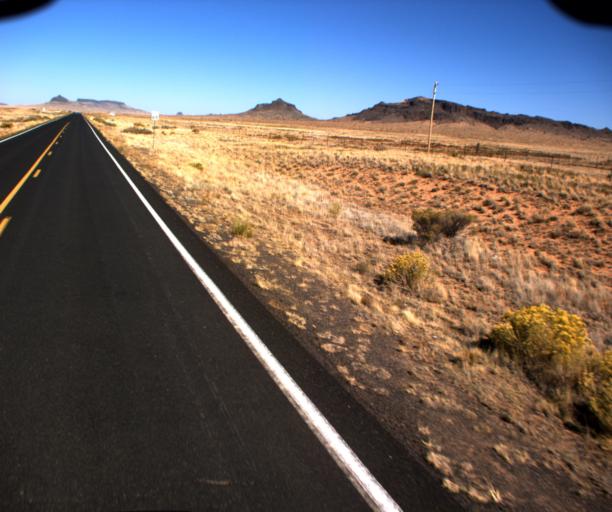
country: US
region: Arizona
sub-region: Navajo County
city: Dilkon
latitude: 35.4491
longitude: -110.4236
